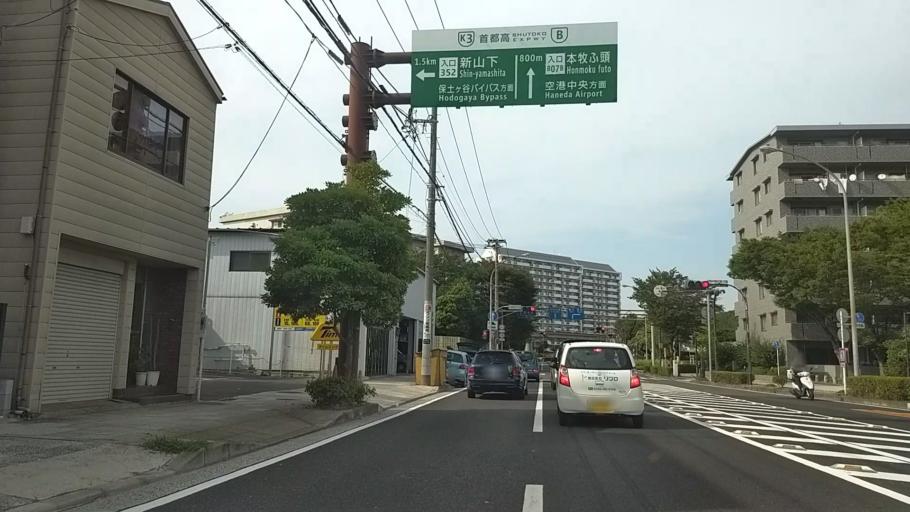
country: JP
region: Kanagawa
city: Yokohama
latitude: 35.4308
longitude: 139.6642
